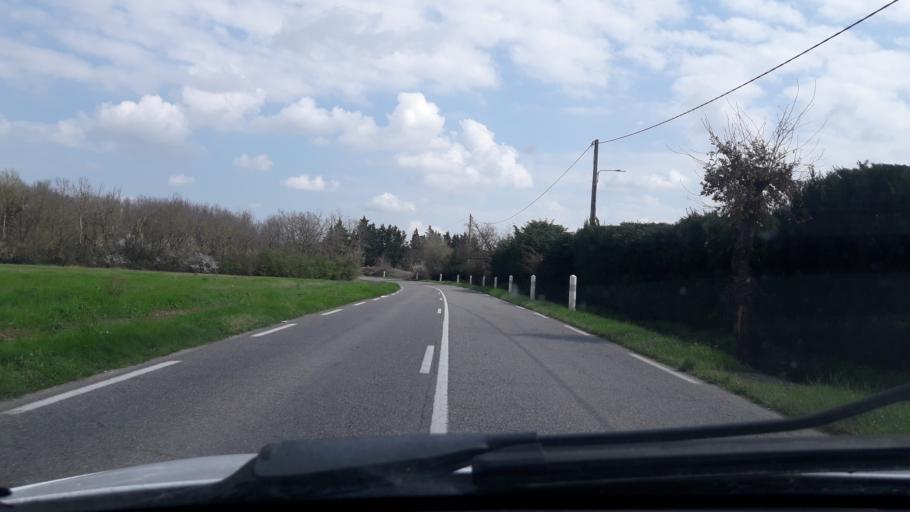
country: FR
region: Midi-Pyrenees
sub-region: Departement de la Haute-Garonne
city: Seysses
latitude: 43.5020
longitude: 1.2685
